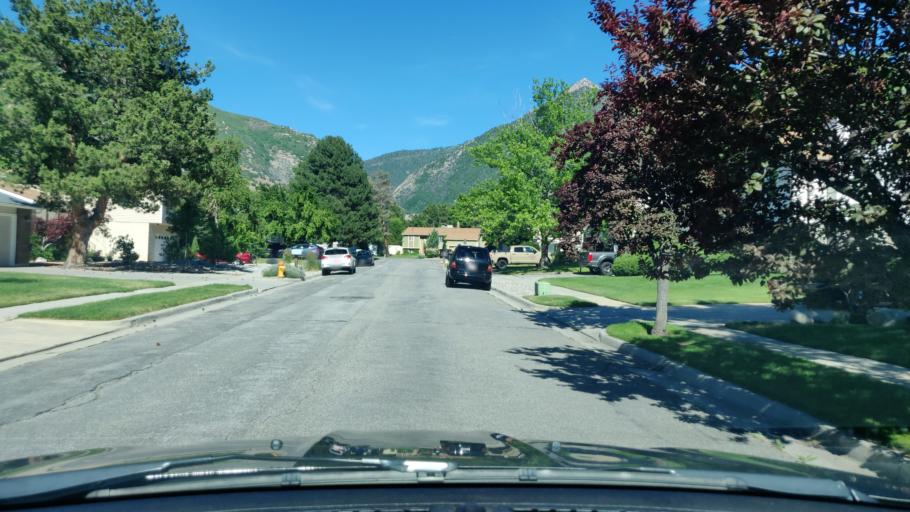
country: US
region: Utah
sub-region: Salt Lake County
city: Cottonwood Heights
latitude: 40.6206
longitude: -111.8039
